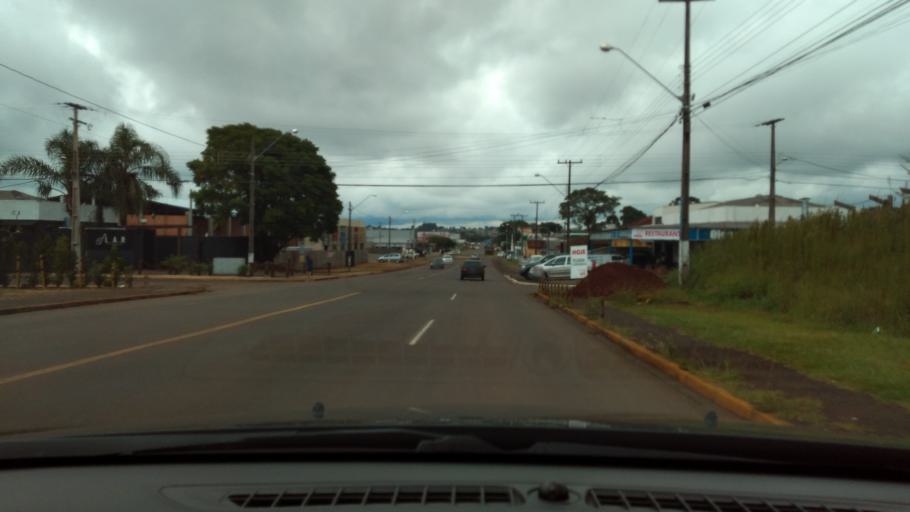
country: BR
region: Parana
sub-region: Guarapuava
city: Guarapuava
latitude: -25.3935
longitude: -51.4907
